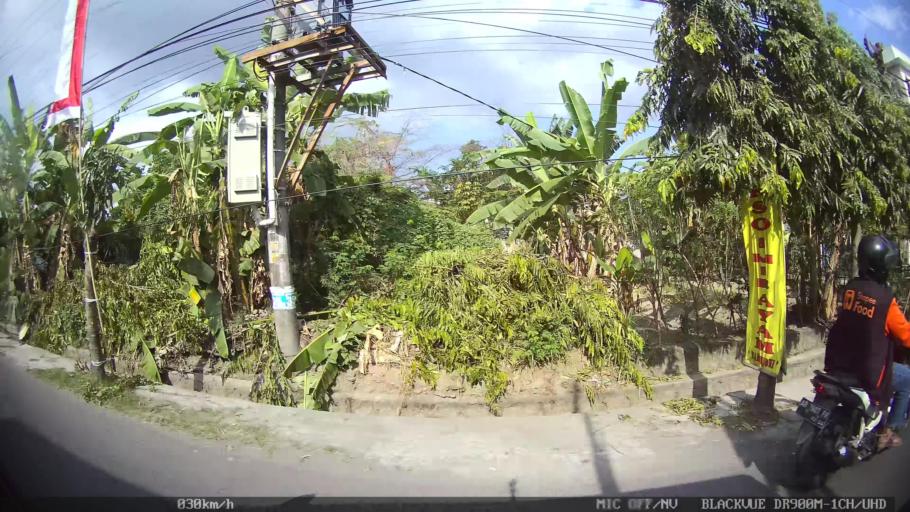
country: ID
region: Daerah Istimewa Yogyakarta
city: Gamping Lor
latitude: -7.7975
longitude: 110.3454
